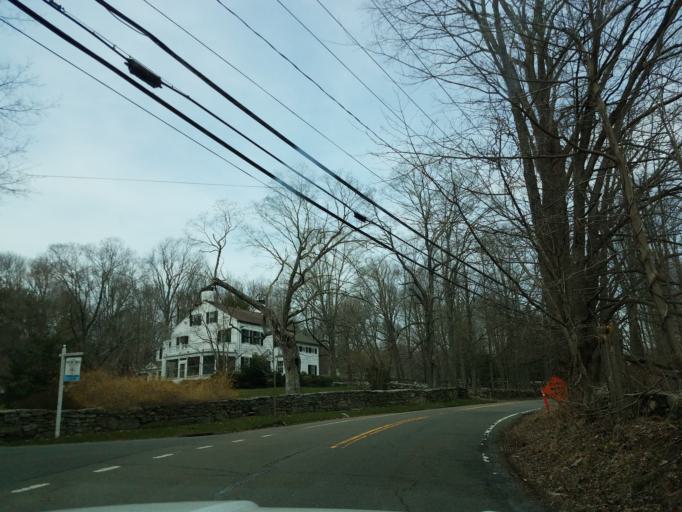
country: US
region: New York
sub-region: Westchester County
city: Armonk
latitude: 41.1087
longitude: -73.6551
